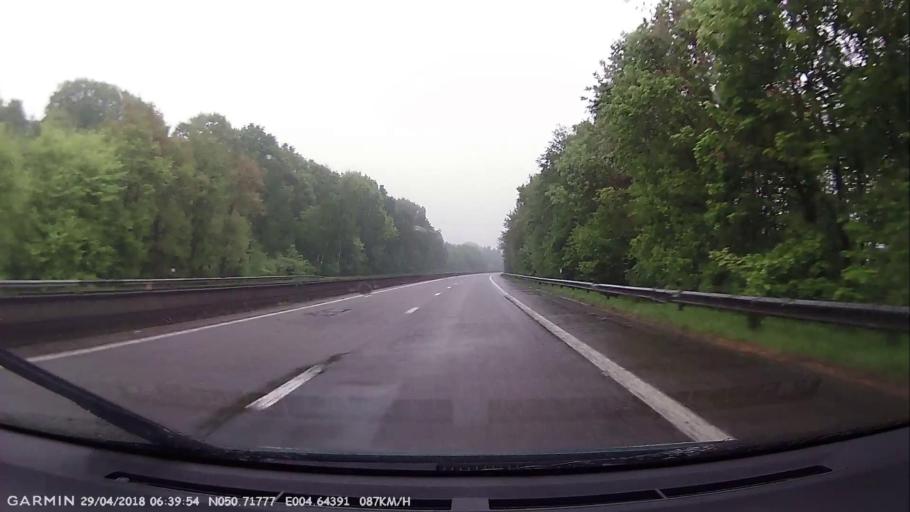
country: BE
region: Wallonia
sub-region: Province du Brabant Wallon
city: Wavre
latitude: 50.7180
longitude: 4.6440
